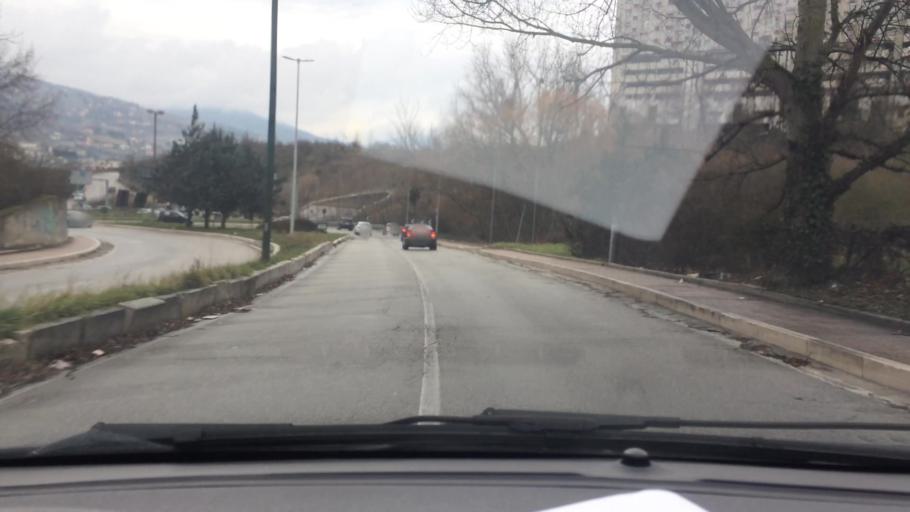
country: IT
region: Basilicate
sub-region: Provincia di Potenza
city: Potenza
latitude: 40.6331
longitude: 15.7940
